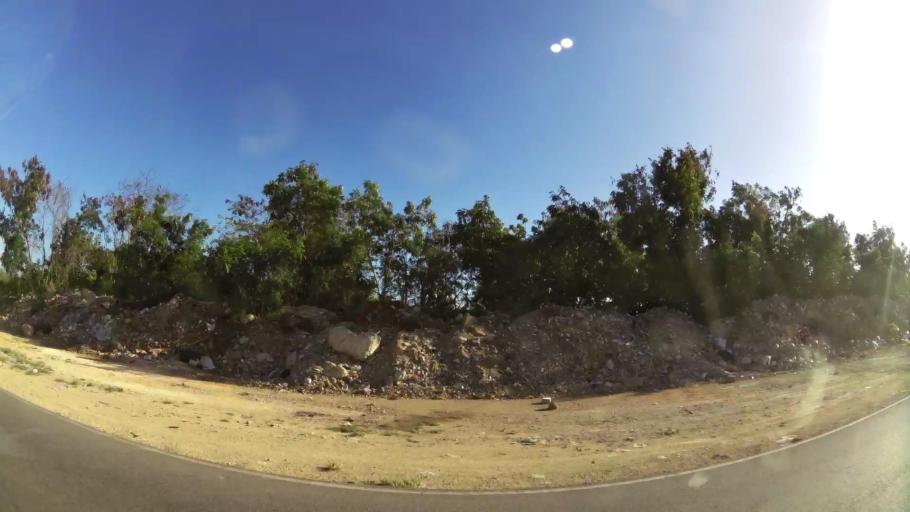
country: DO
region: Santo Domingo
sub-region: Santo Domingo
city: Santo Domingo Este
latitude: 18.4827
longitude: -69.8167
